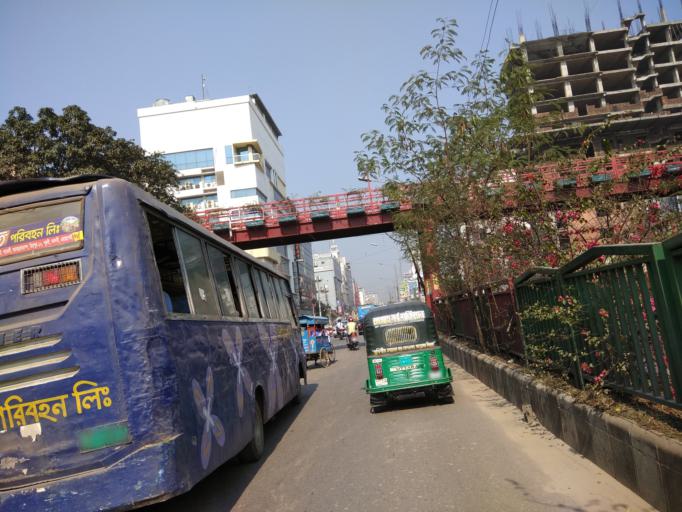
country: BD
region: Dhaka
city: Tungi
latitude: 23.8139
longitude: 90.3668
